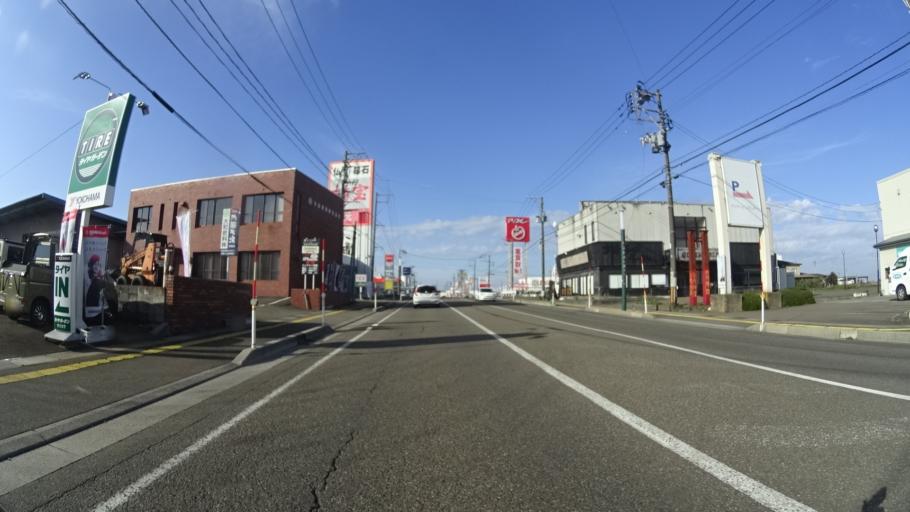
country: JP
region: Niigata
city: Joetsu
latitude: 37.1332
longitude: 138.2436
